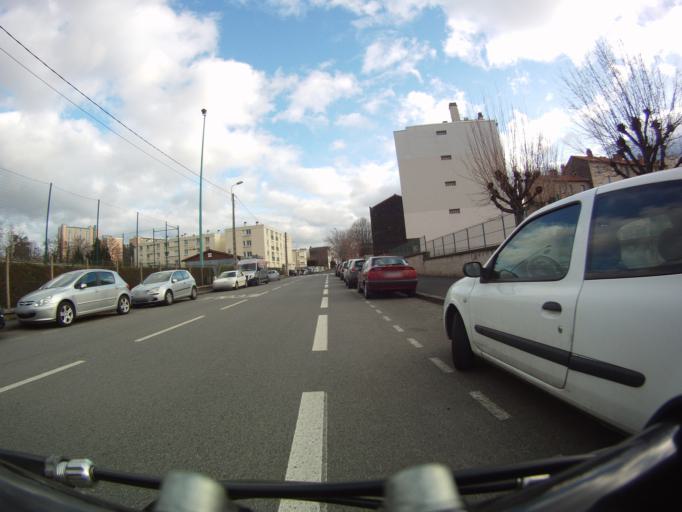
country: FR
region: Auvergne
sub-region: Departement du Puy-de-Dome
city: Beaumont
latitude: 45.7627
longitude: 3.0849
